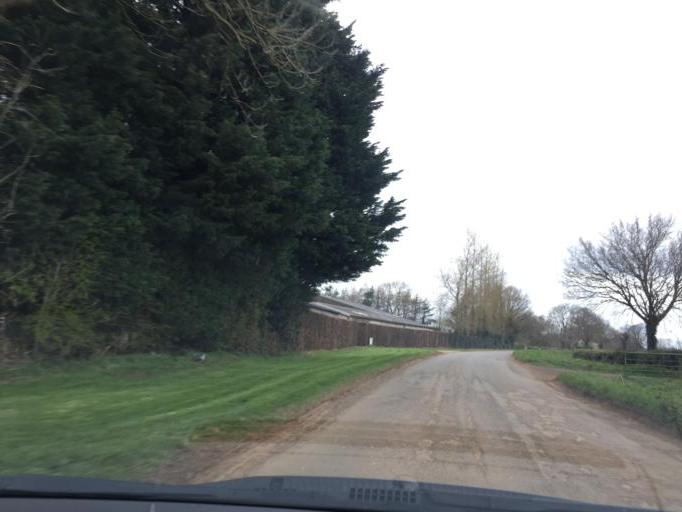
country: GB
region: England
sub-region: Oxfordshire
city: Hanwell
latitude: 52.0972
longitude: -1.4002
